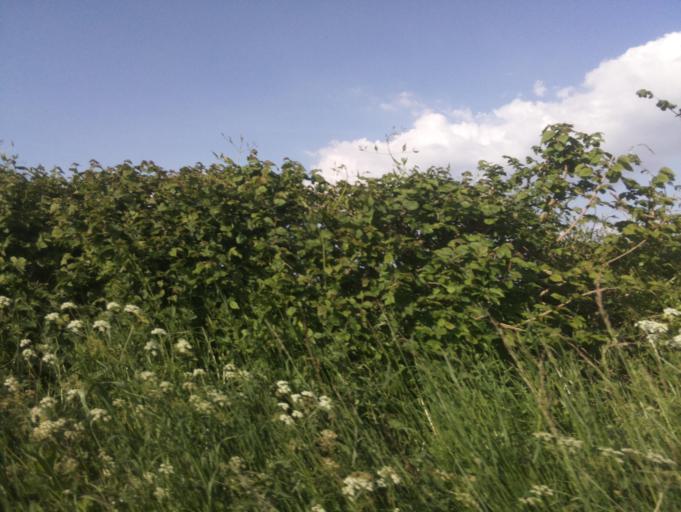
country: GB
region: England
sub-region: Wiltshire
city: Biddestone
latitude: 51.4939
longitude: -2.1975
